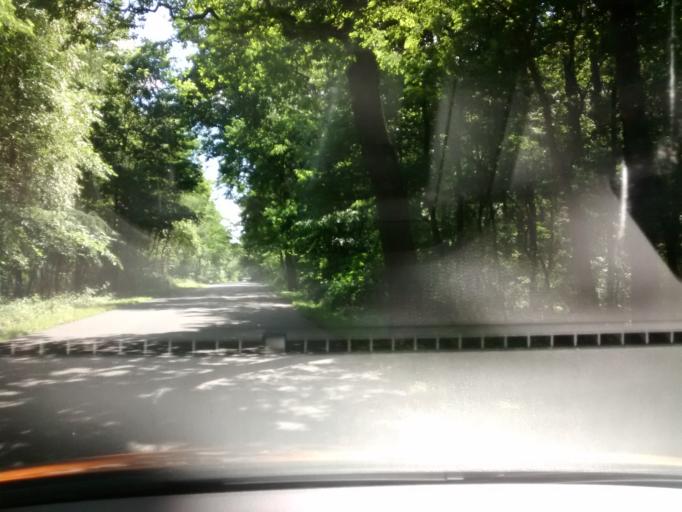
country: DE
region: Berlin
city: Kladow
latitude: 52.4917
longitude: 13.1241
